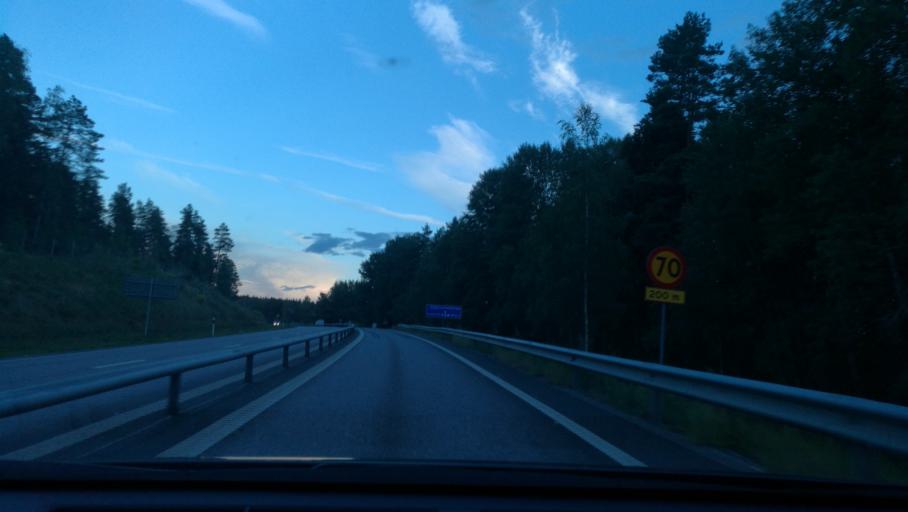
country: SE
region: Soedermanland
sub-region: Katrineholms Kommun
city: Katrineholm
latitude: 58.9083
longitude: 16.1991
